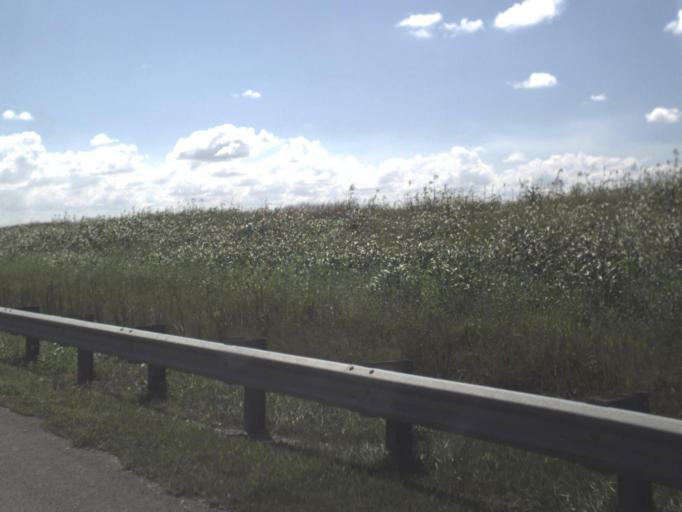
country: US
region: Florida
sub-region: Glades County
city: Moore Haven
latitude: 26.8747
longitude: -81.1227
